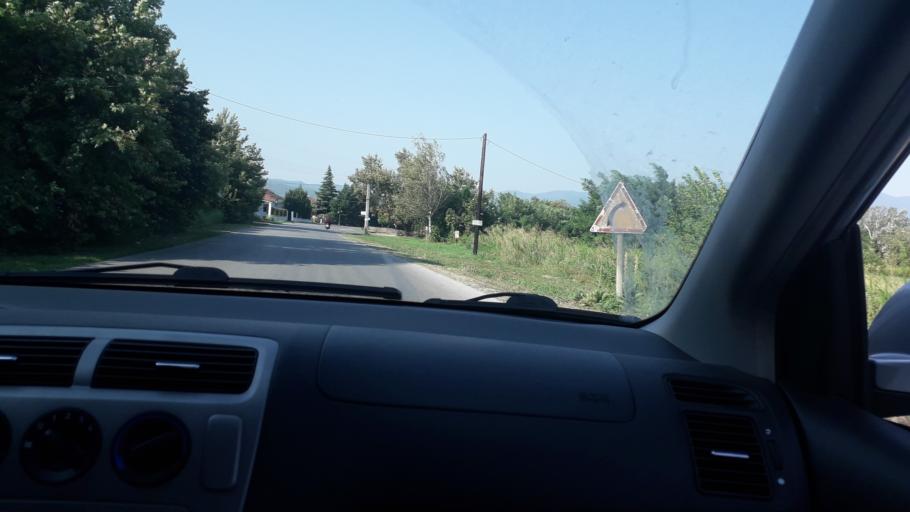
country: GR
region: Central Macedonia
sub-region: Nomos Pellis
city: Tsakoi
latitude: 40.9573
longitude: 22.0451
